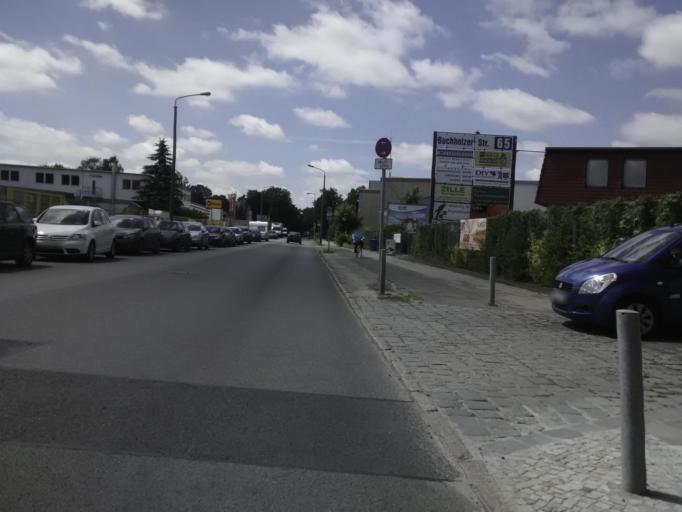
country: DE
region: Berlin
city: Niederschonhausen
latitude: 52.5895
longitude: 13.4146
